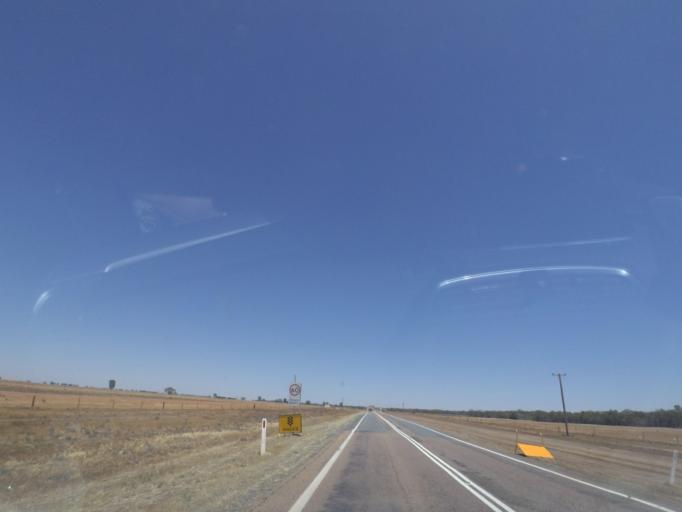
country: AU
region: New South Wales
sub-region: Berrigan
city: Berrigan
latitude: -35.1495
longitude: 145.9949
